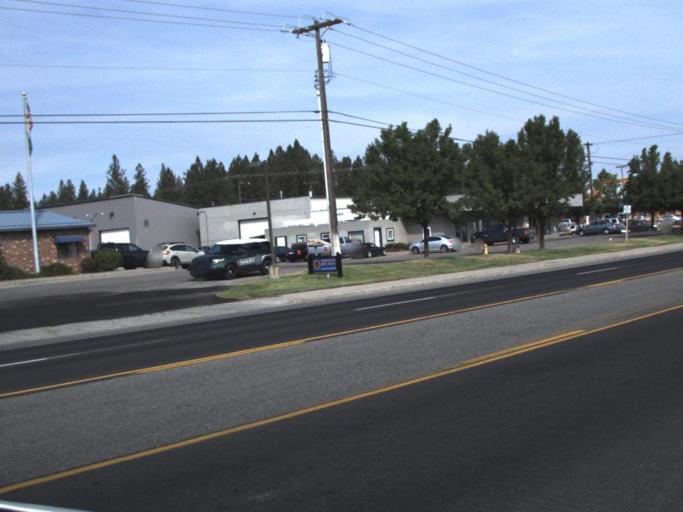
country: US
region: Washington
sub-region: Spokane County
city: Fairwood
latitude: 47.7681
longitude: -117.4049
